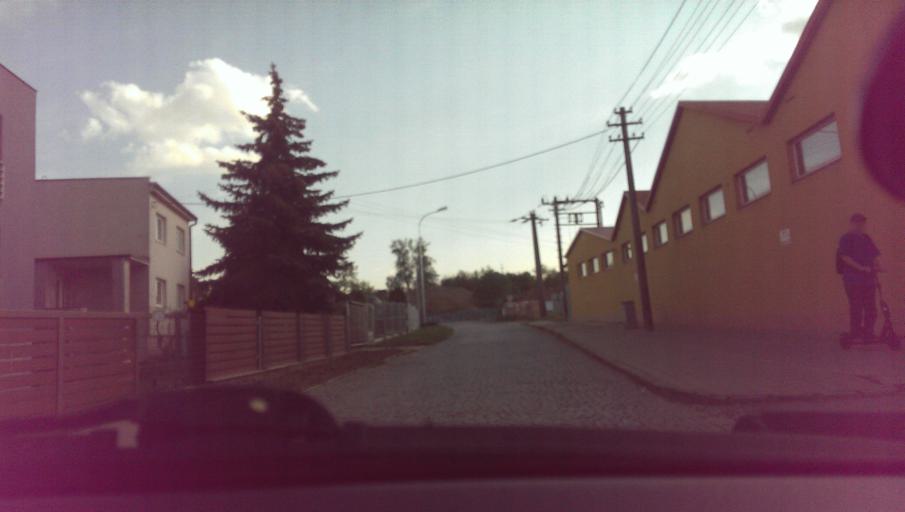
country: CZ
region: Zlin
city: Uhersky Brod
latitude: 49.0169
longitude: 17.6445
